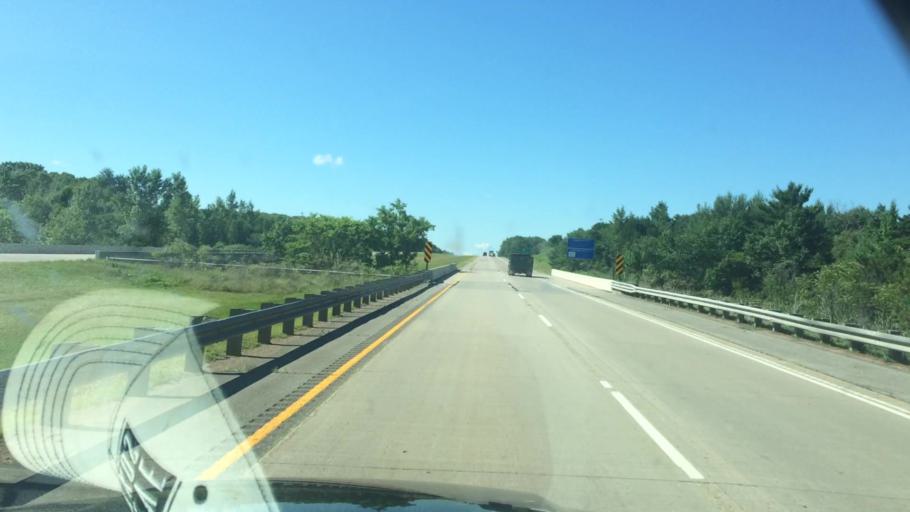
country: US
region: Wisconsin
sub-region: Marathon County
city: Mosinee
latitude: 44.6848
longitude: -89.6414
